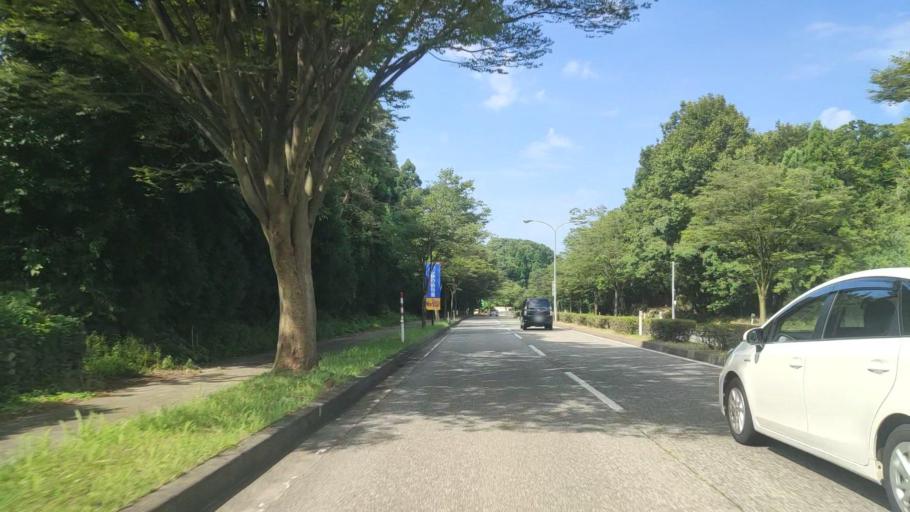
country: JP
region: Ishikawa
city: Matsuto
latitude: 36.4482
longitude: 136.5611
